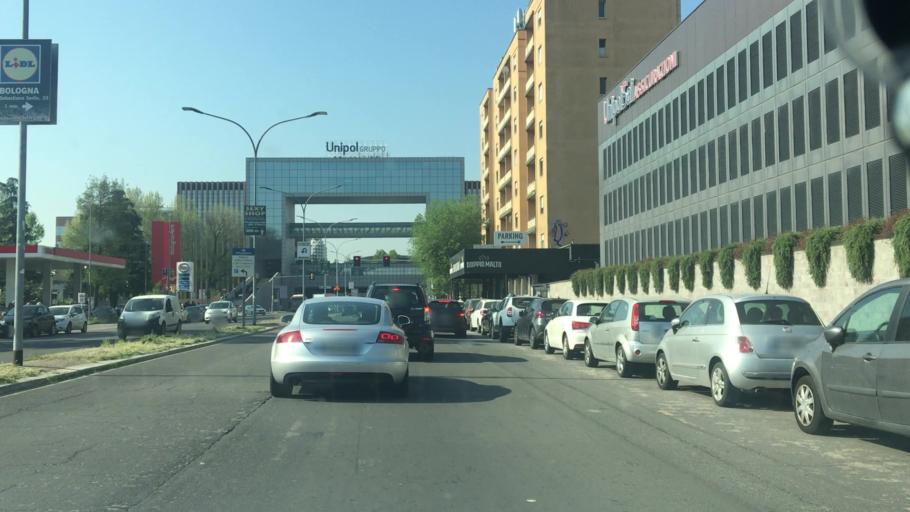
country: IT
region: Emilia-Romagna
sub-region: Provincia di Bologna
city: Bologna
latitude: 44.5140
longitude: 11.3584
